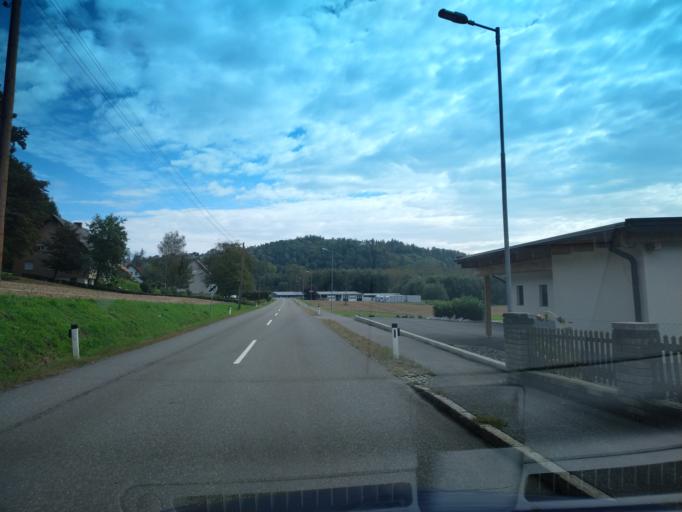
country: AT
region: Styria
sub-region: Politischer Bezirk Leibnitz
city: Seggauberg
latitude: 46.7768
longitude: 15.5030
